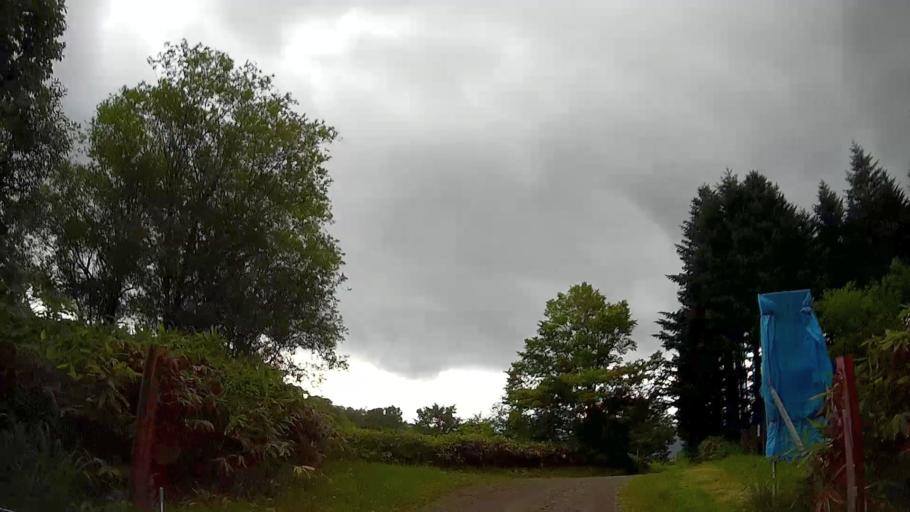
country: JP
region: Hokkaido
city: Nanae
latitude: 42.1255
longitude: 140.4177
